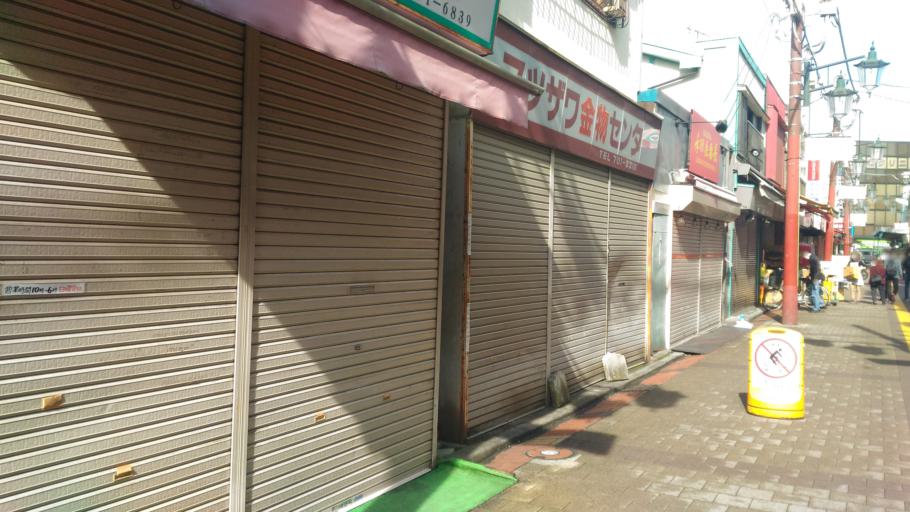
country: JP
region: Kanagawa
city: Zushi
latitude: 35.3426
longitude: 139.6221
